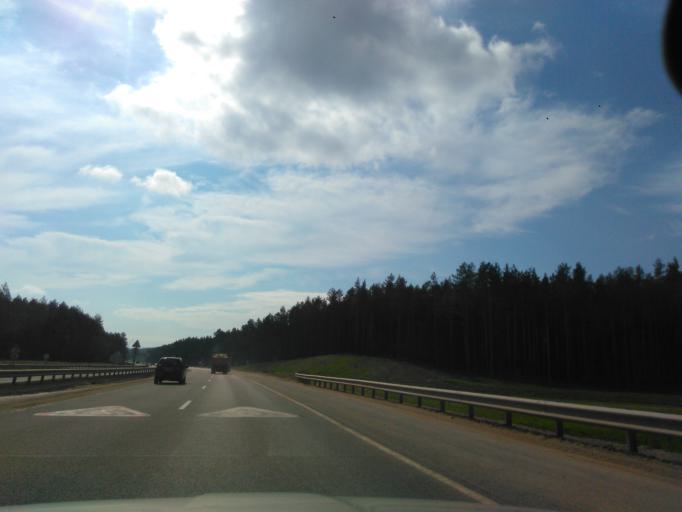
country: BY
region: Minsk
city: Rakaw
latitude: 53.9644
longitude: 27.0901
